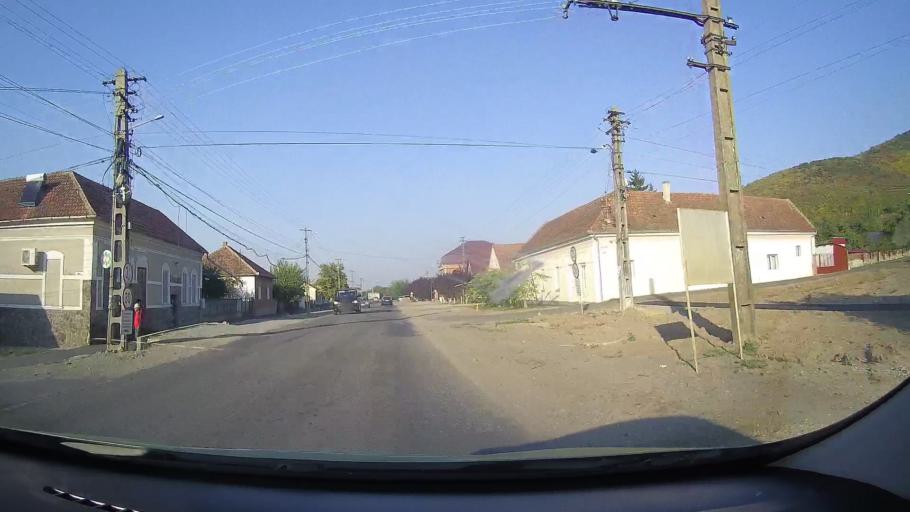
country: RO
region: Arad
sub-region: Comuna Siria
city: Siria
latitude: 46.2734
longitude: 21.6407
